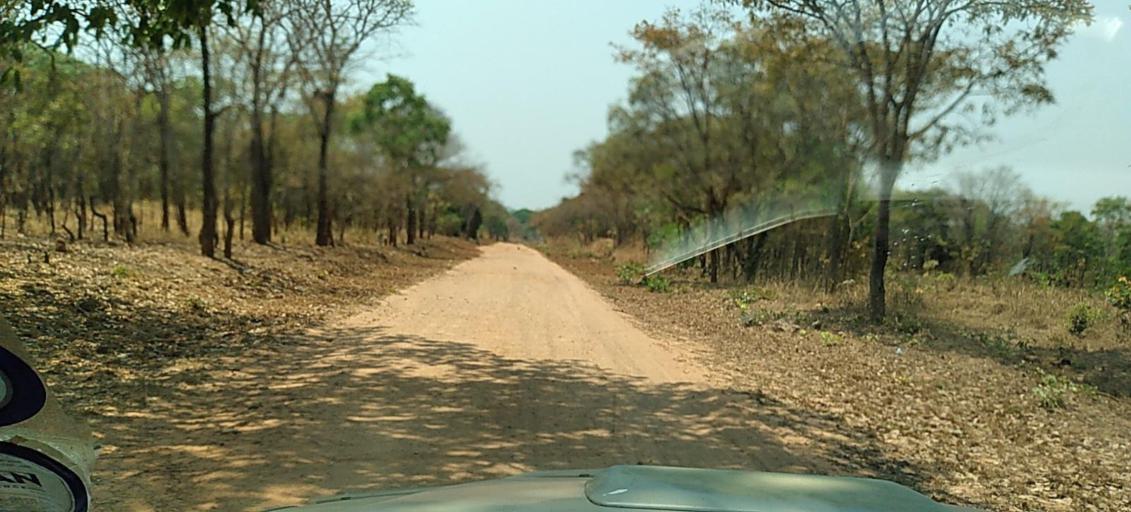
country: ZM
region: North-Western
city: Kasempa
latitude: -13.5509
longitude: 26.0169
